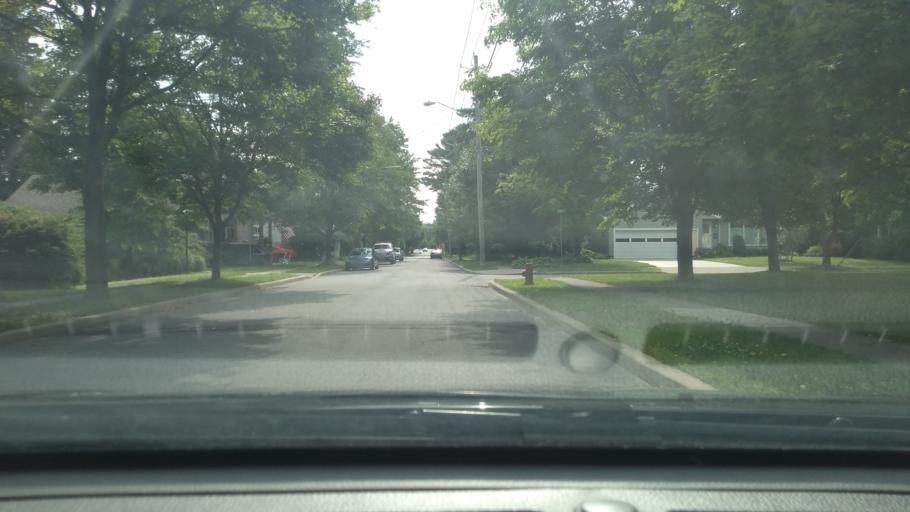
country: US
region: New York
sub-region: Erie County
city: East Aurora
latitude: 42.7733
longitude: -78.6189
